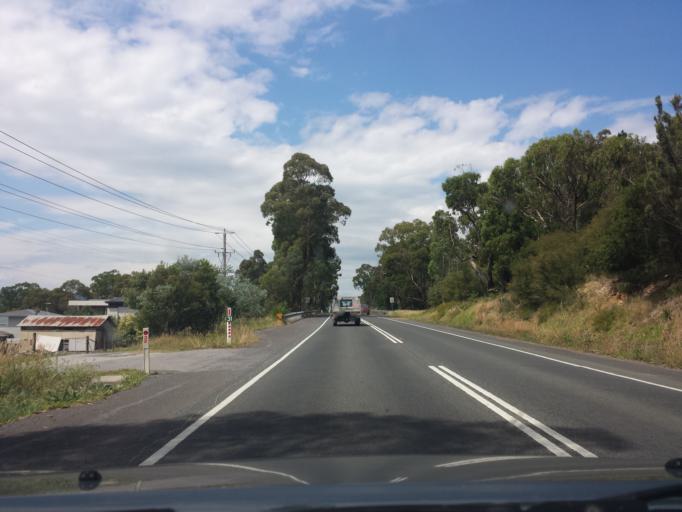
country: AU
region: Victoria
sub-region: Yarra Ranges
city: Lysterfield
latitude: -37.9268
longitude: 145.2783
